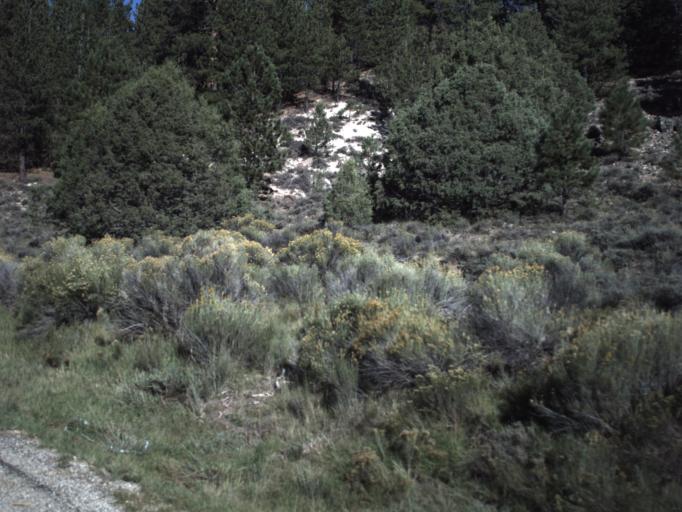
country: US
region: Utah
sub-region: Garfield County
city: Panguitch
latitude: 37.7296
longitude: -112.6066
